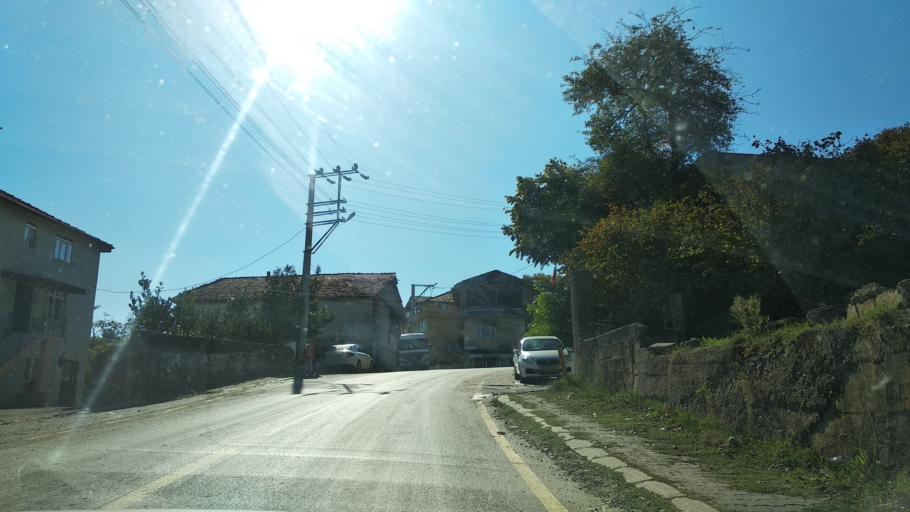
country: TR
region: Sakarya
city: Karasu
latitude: 41.1036
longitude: 30.6345
